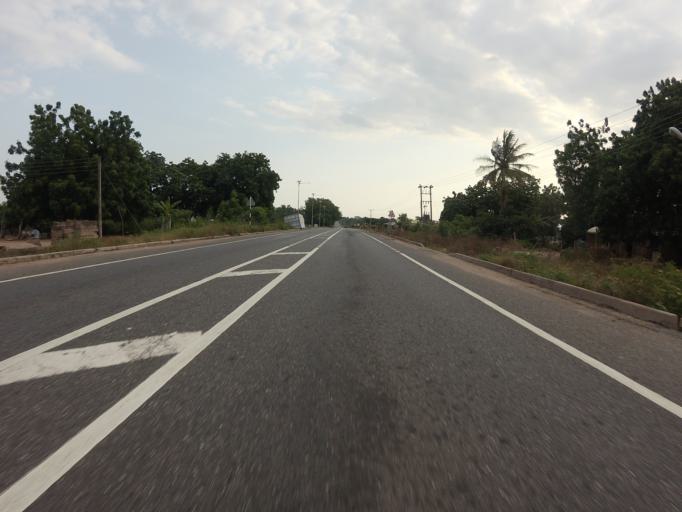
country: GH
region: Volta
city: Anloga
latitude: 6.1041
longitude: 0.5139
